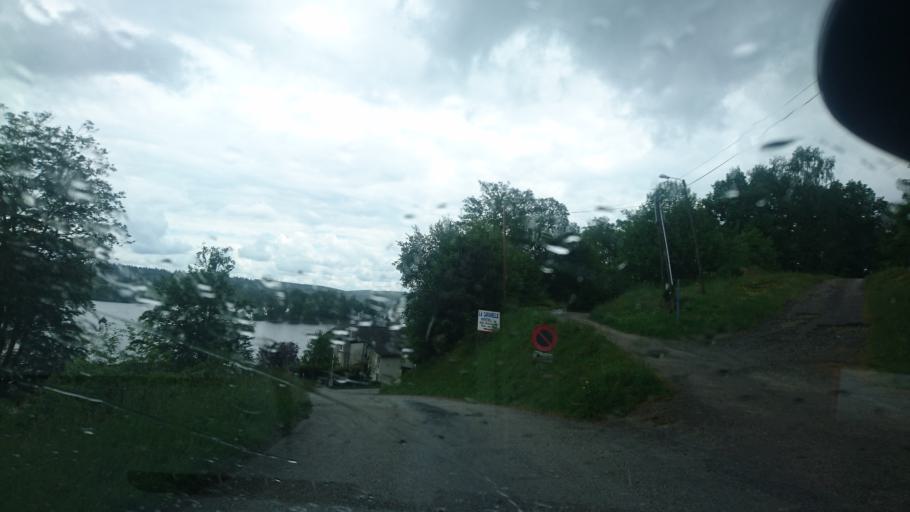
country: FR
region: Limousin
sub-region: Departement de la Haute-Vienne
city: Peyrat-le-Chateau
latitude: 45.8023
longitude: 1.8439
